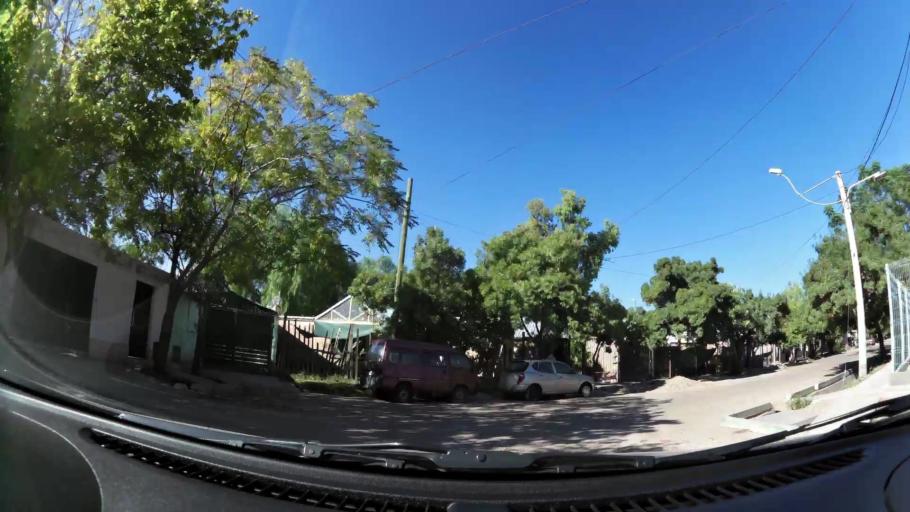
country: AR
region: Mendoza
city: Las Heras
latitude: -32.8729
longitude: -68.8667
